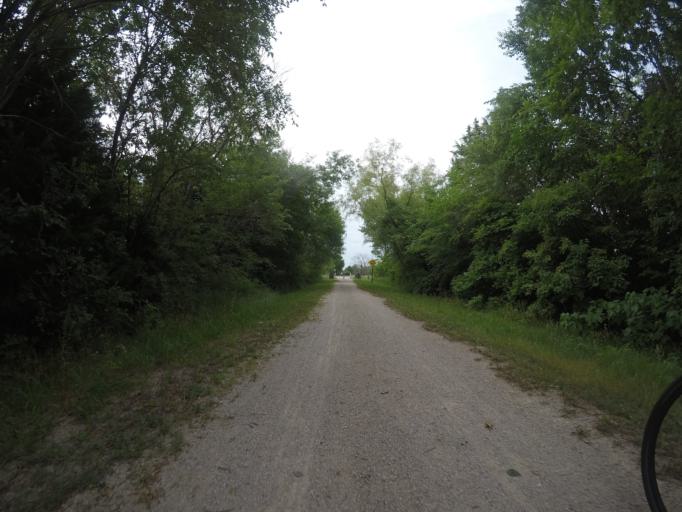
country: US
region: Kansas
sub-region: Franklin County
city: Ottawa
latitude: 38.4927
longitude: -95.2741
